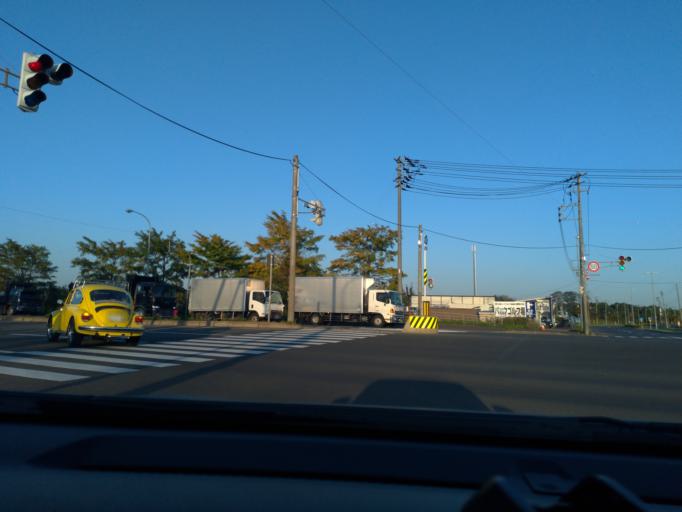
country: JP
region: Hokkaido
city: Ishikari
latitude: 43.1570
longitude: 141.4137
